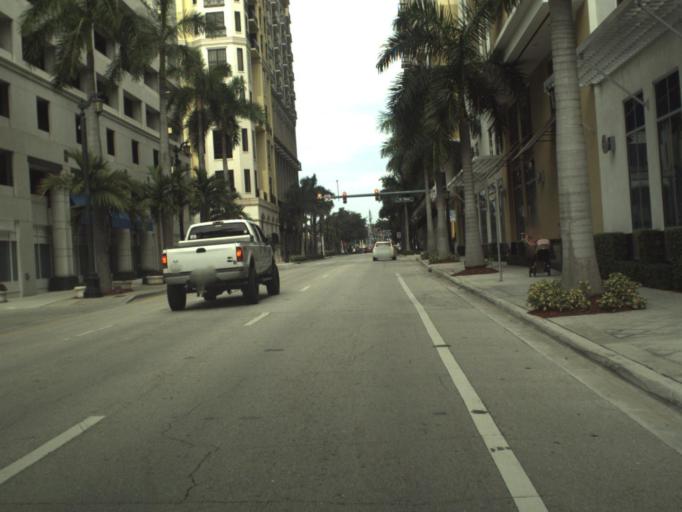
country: US
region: Florida
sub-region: Palm Beach County
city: West Palm Beach
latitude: 26.7063
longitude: -80.0512
